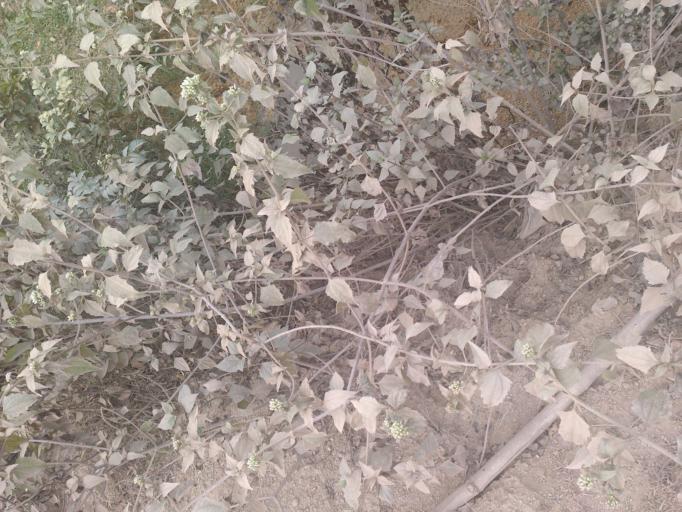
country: LA
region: Xiangkhoang
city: Muang Phonsavan
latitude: 19.3414
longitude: 103.5627
